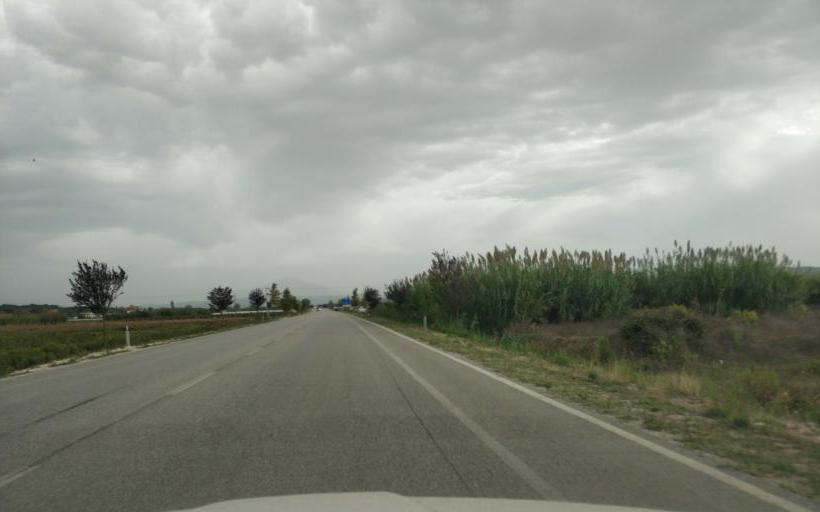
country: AL
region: Fier
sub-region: Rrethi i Fierit
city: Frakulla e Madhe
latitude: 40.6356
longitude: 19.5049
